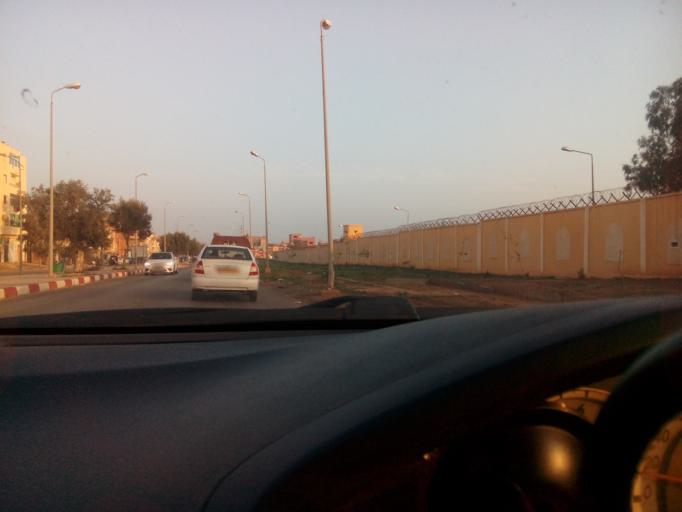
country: DZ
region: Oran
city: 'Ain el Turk
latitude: 35.7348
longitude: -0.7723
